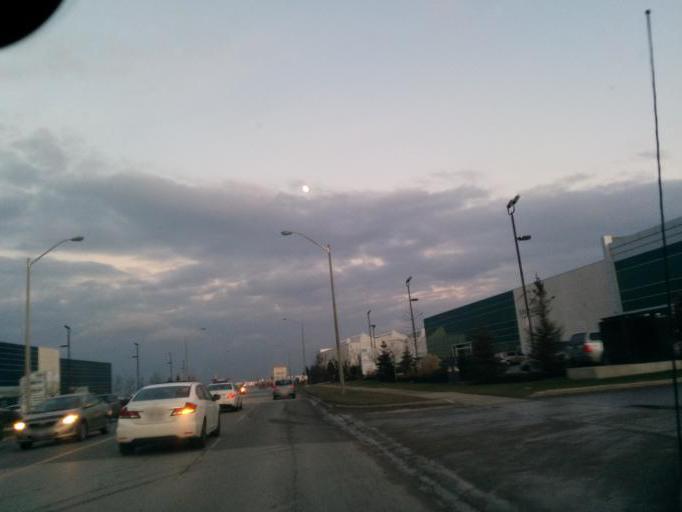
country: CA
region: Ontario
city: Etobicoke
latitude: 43.7753
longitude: -79.6416
